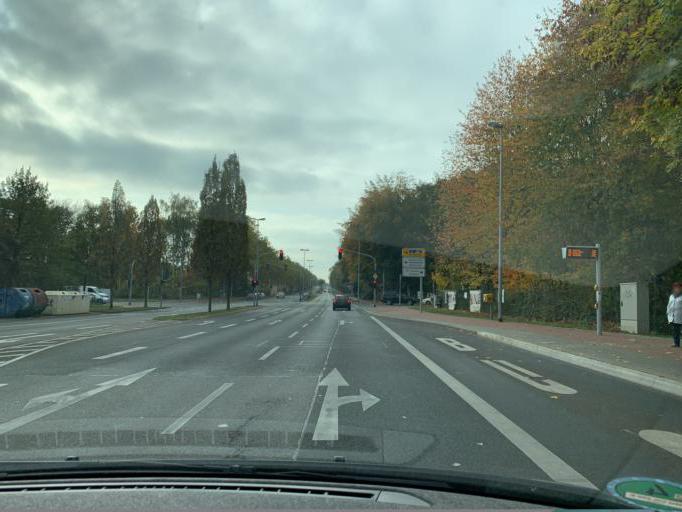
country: DE
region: North Rhine-Westphalia
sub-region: Regierungsbezirk Dusseldorf
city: Monchengladbach
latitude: 51.1497
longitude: 6.4323
